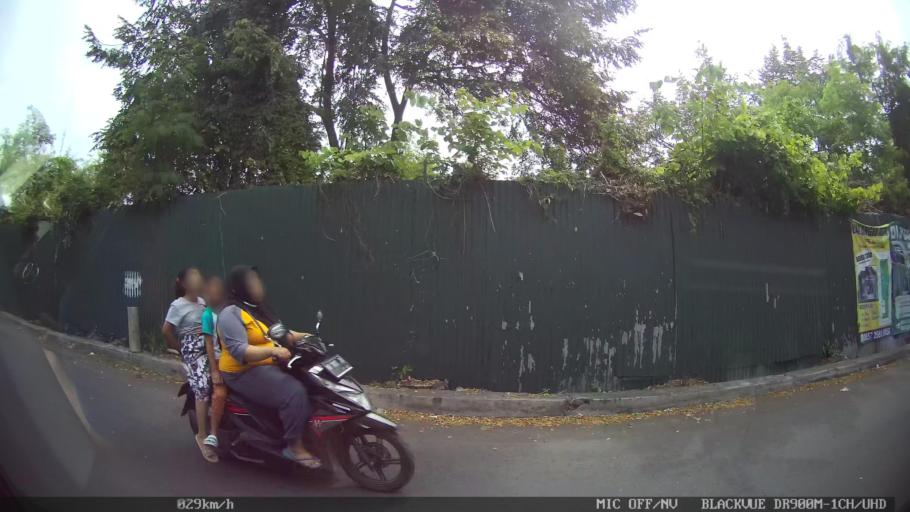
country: ID
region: Daerah Istimewa Yogyakarta
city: Depok
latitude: -7.7507
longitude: 110.4488
